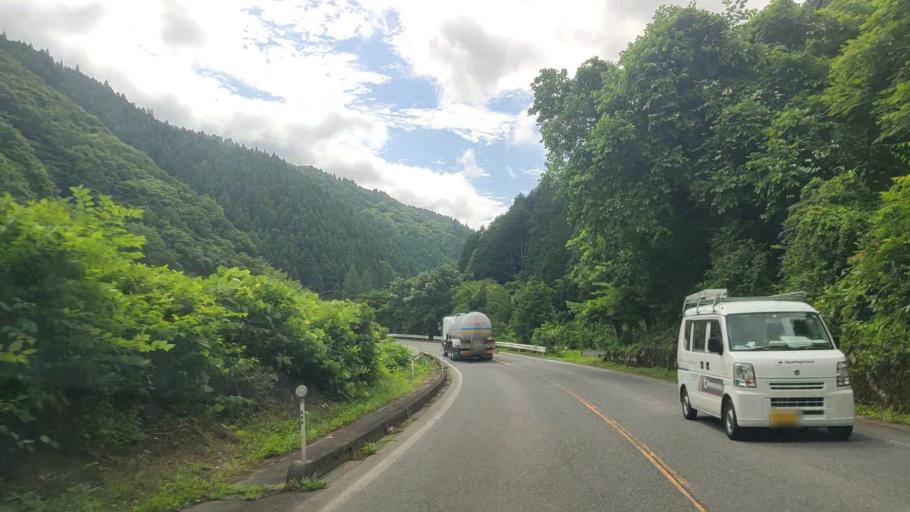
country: JP
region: Tottori
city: Yonago
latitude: 35.2318
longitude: 133.4404
